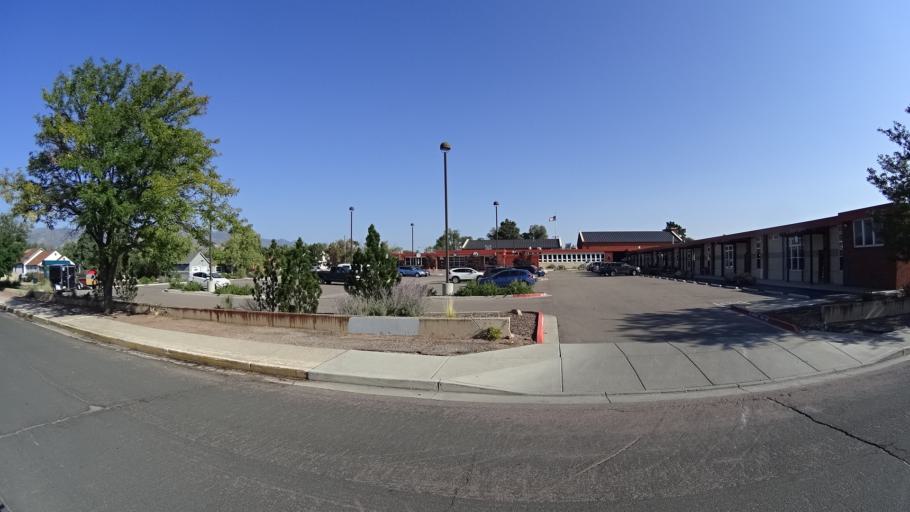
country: US
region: Colorado
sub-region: El Paso County
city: Colorado Springs
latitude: 38.8706
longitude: -104.8224
